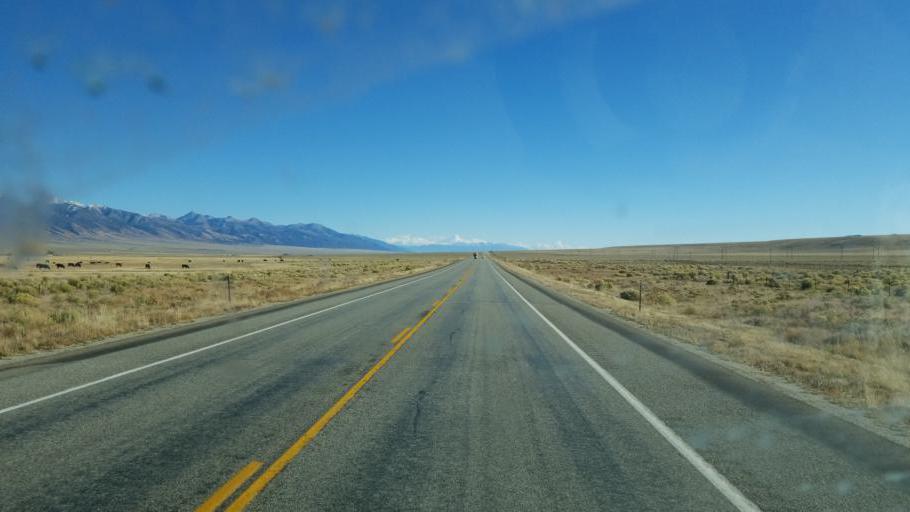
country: US
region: Colorado
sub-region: Chaffee County
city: Salida
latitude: 38.3188
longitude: -106.0023
